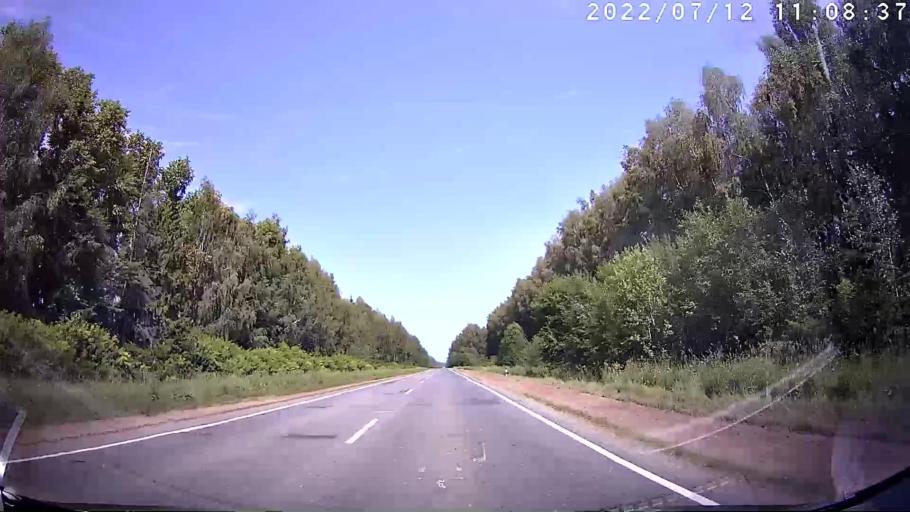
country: RU
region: Mariy-El
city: Kuzhener
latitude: 56.8918
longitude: 48.7541
